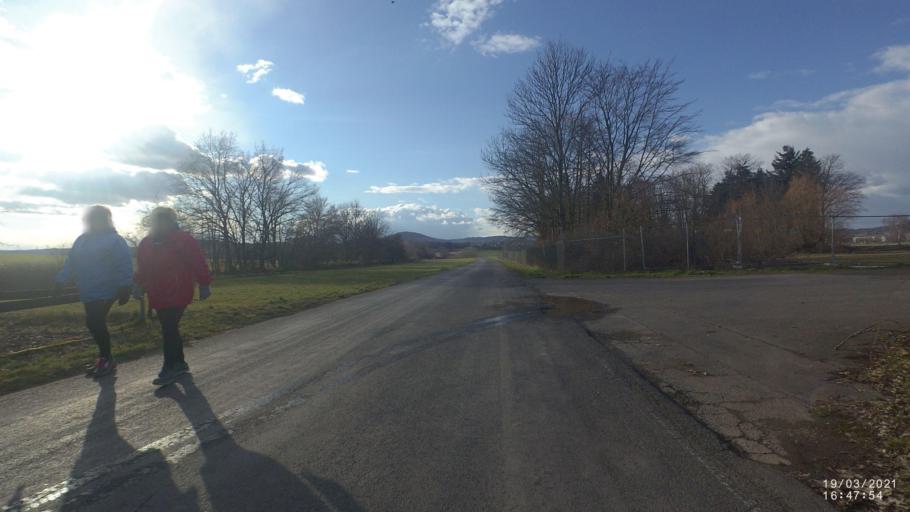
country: DE
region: Rheinland-Pfalz
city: Thur
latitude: 50.3580
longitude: 7.3028
